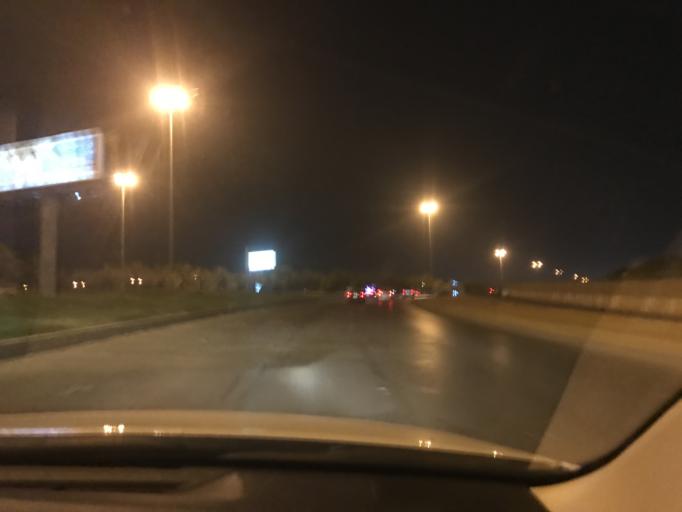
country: SA
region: Ar Riyad
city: Riyadh
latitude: 24.7928
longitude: 46.7252
